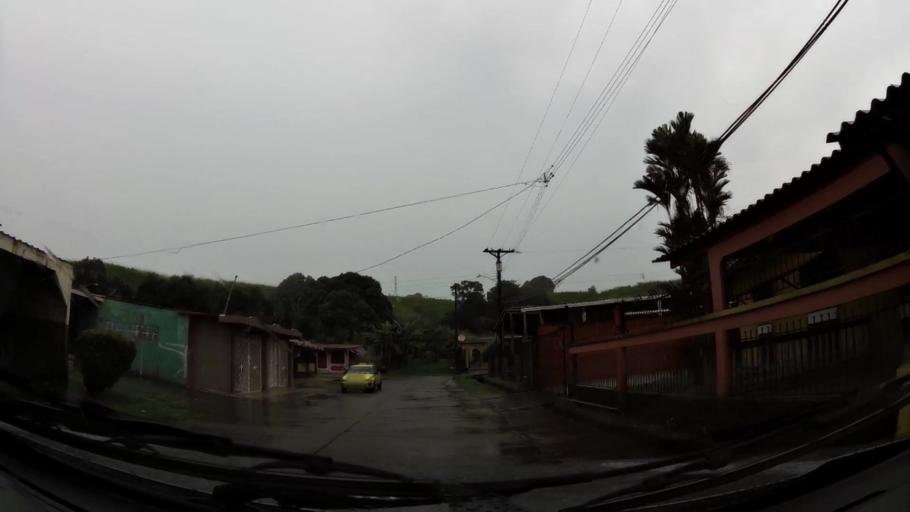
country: PA
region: Colon
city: Sabanitas
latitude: 9.3561
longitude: -79.8149
